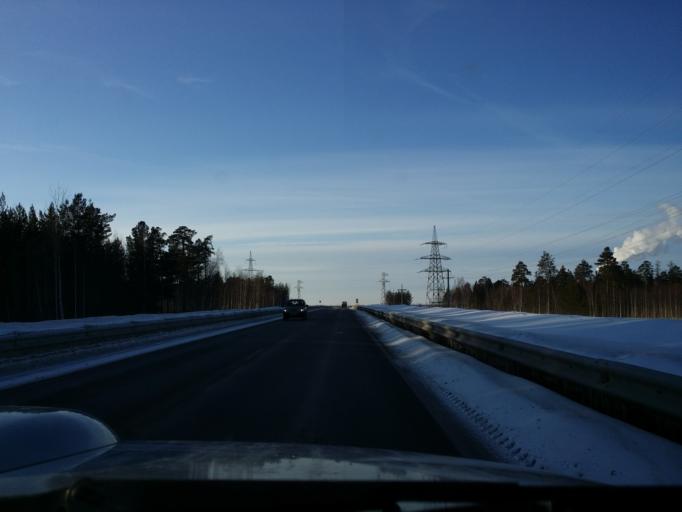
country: RU
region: Khanty-Mansiyskiy Avtonomnyy Okrug
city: Izluchinsk
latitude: 60.9315
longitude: 76.9877
